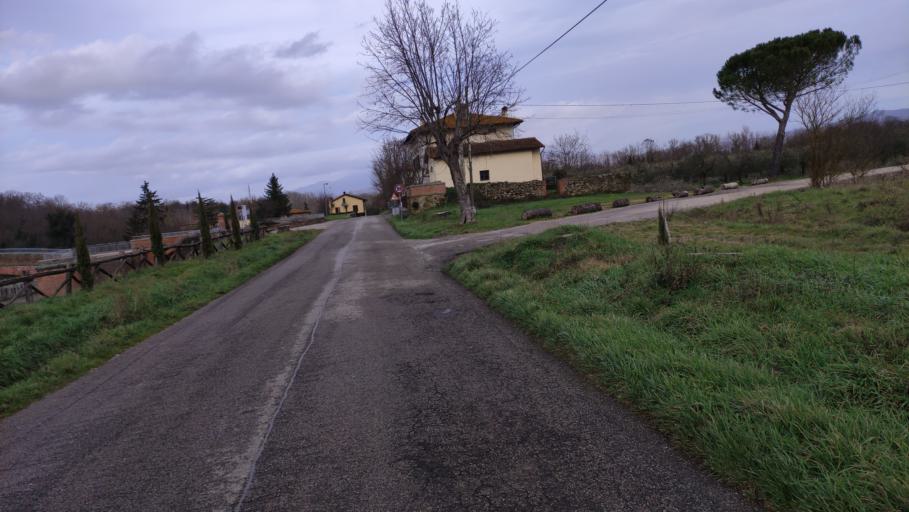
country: IT
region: Tuscany
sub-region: Province of Arezzo
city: Pratantico-Indicatore
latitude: 43.4671
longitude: 11.8251
